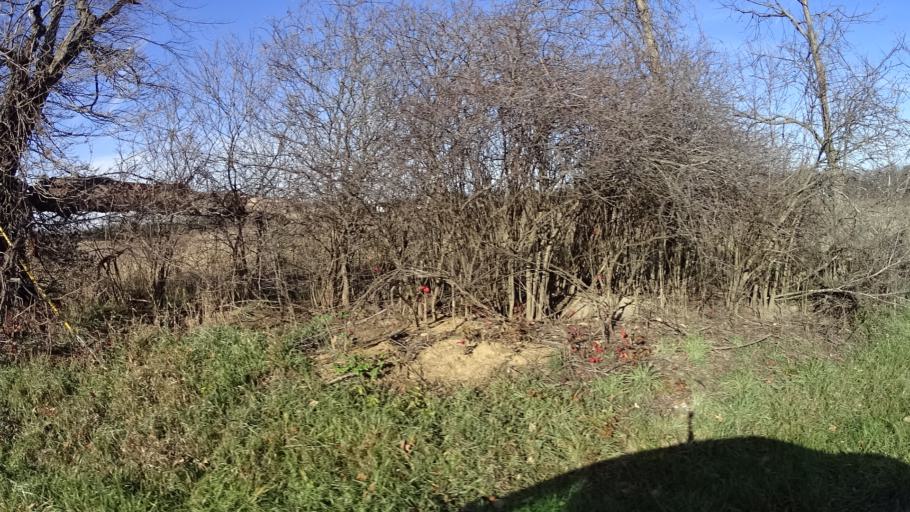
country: US
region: Ohio
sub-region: Lorain County
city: Wellington
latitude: 41.1156
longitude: -82.3014
